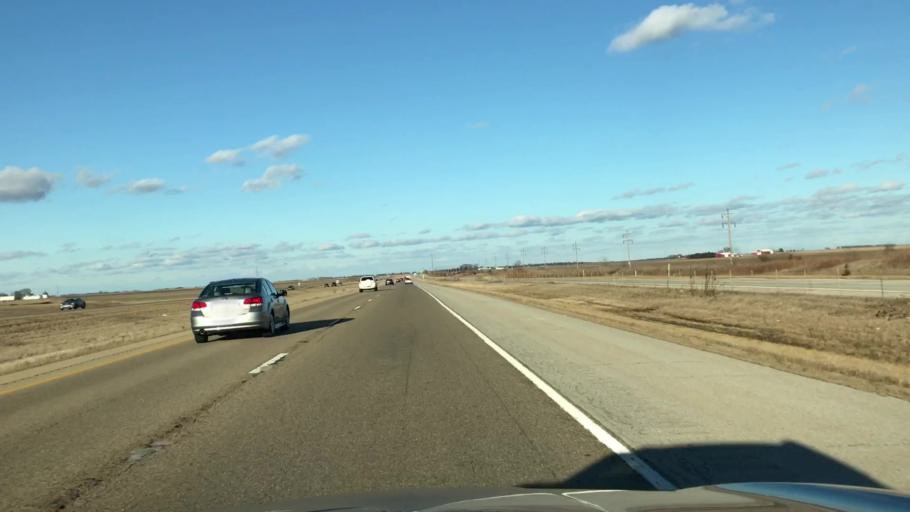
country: US
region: Illinois
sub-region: McLean County
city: Chenoa
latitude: 40.7015
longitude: -88.7485
